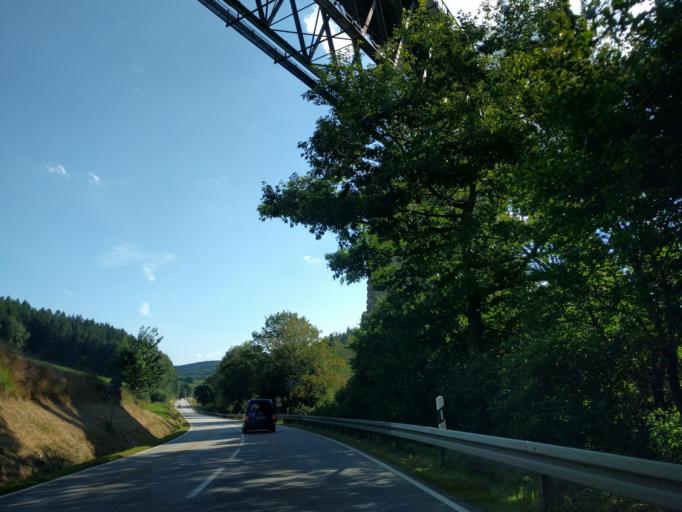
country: DE
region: Bavaria
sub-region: Lower Bavaria
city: Regen
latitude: 48.9635
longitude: 13.1033
